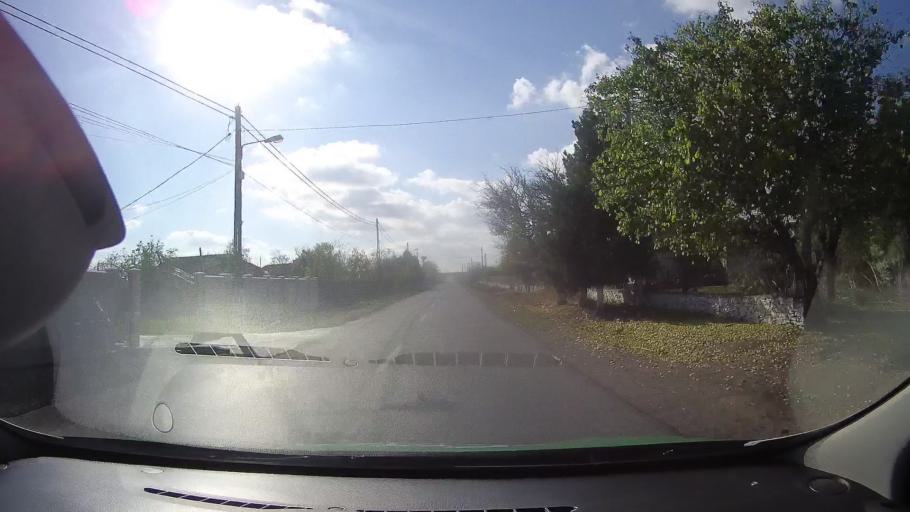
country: RO
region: Constanta
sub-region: Comuna Mihai Viteazu
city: Mihai Viteazu
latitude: 44.6242
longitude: 28.7306
